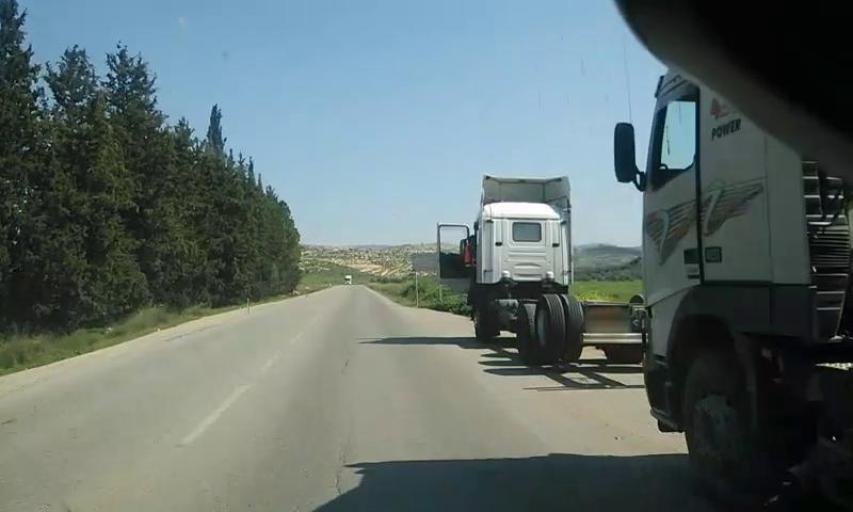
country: PS
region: West Bank
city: Idhna
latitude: 31.5899
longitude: 34.9671
